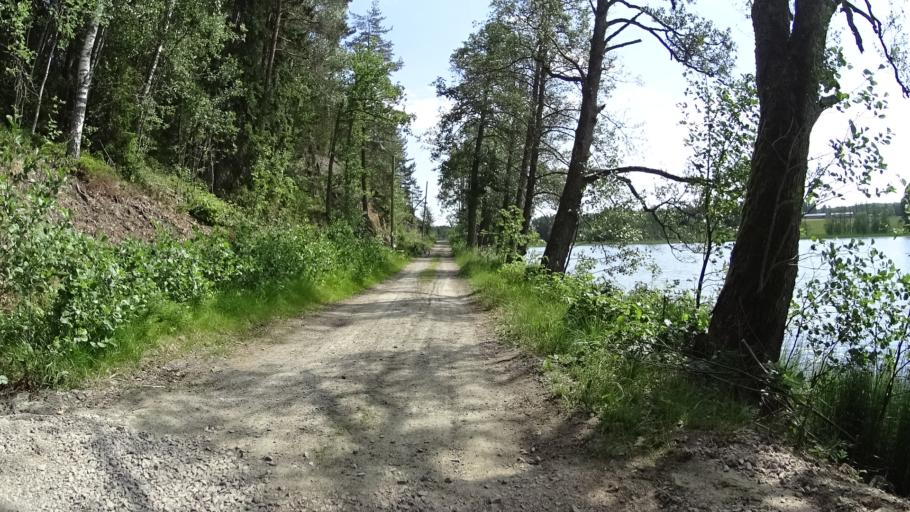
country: FI
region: Uusimaa
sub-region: Raaseporin
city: Pohja
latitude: 60.1129
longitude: 23.5440
